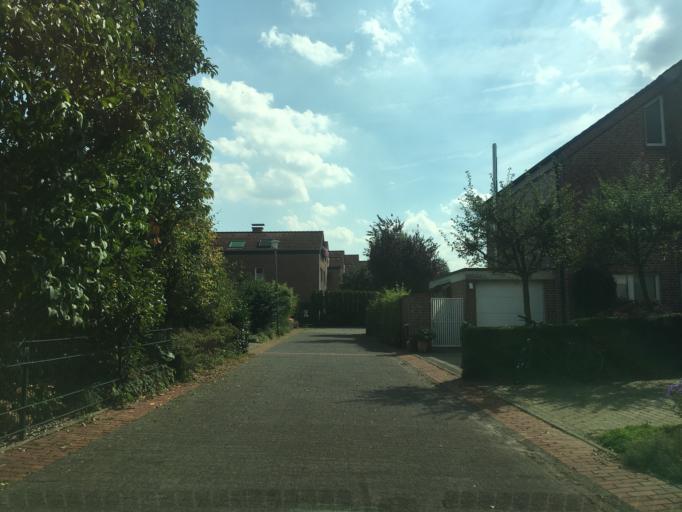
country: DE
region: North Rhine-Westphalia
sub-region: Regierungsbezirk Munster
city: Muenster
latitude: 51.9823
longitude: 7.6531
